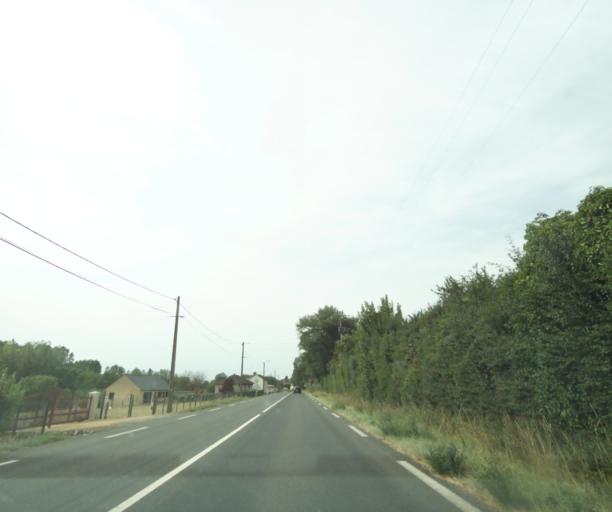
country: FR
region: Centre
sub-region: Departement d'Indre-et-Loire
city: Saint-Christophe-sur-le-Nais
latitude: 47.6607
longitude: 0.4768
